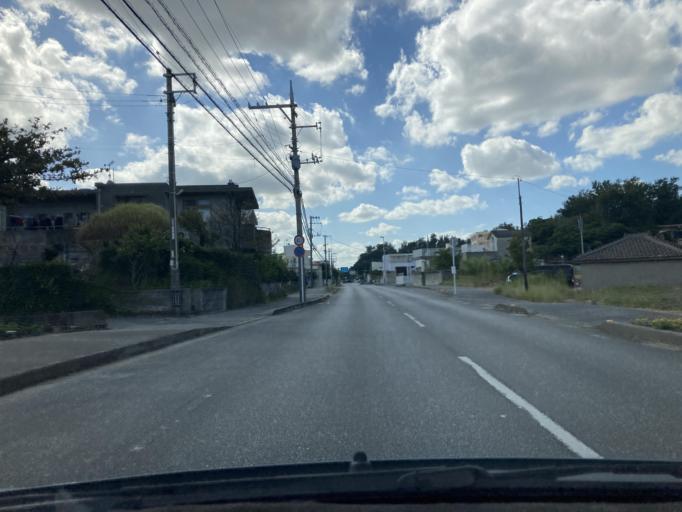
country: JP
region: Okinawa
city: Gushikawa
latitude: 26.3421
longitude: 127.8468
